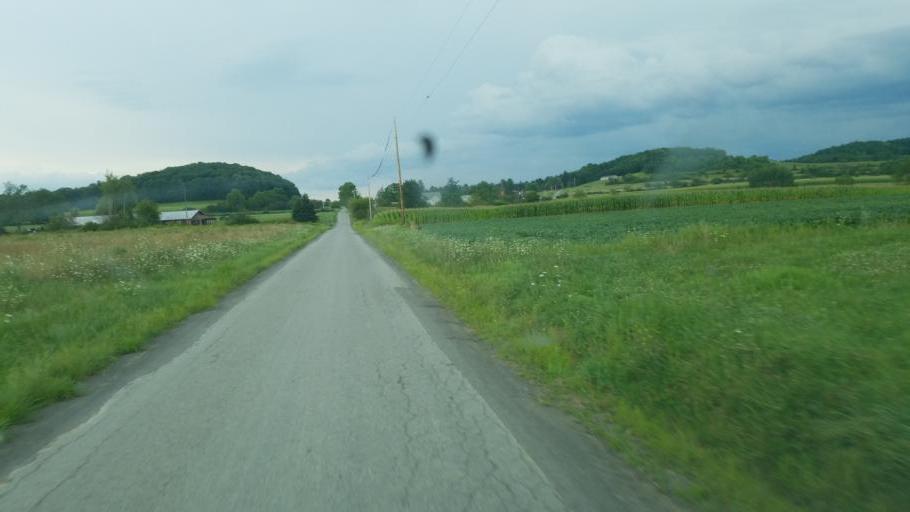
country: US
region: Pennsylvania
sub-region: Clarion County
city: Knox
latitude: 41.2571
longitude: -79.5610
